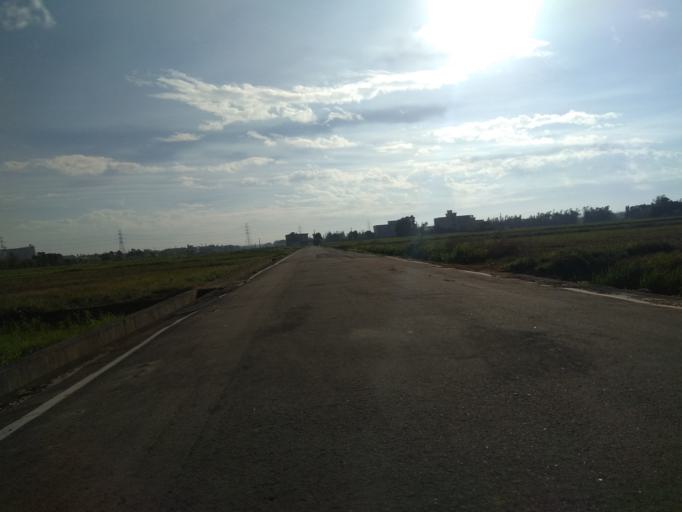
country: TW
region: Taiwan
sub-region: Hsinchu
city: Zhubei
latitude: 24.9797
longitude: 121.0585
